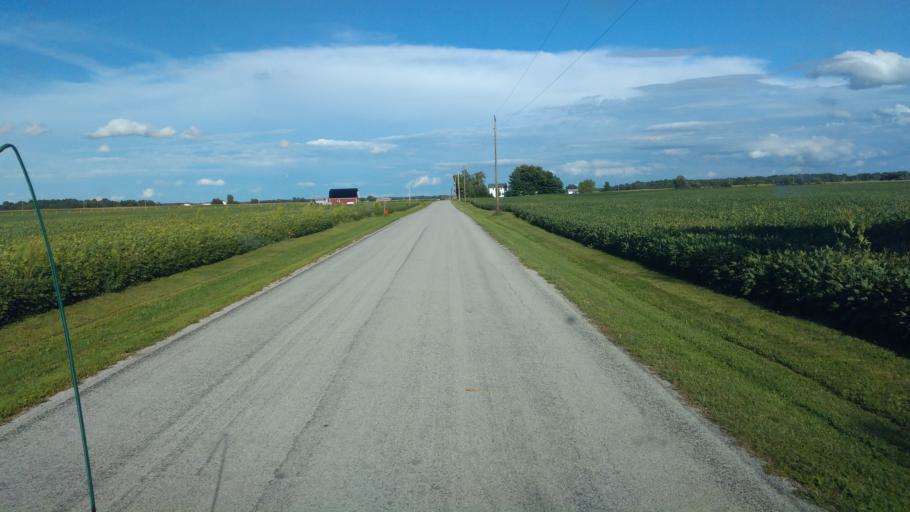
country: US
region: Ohio
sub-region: Hardin County
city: Kenton
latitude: 40.7613
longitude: -83.6645
